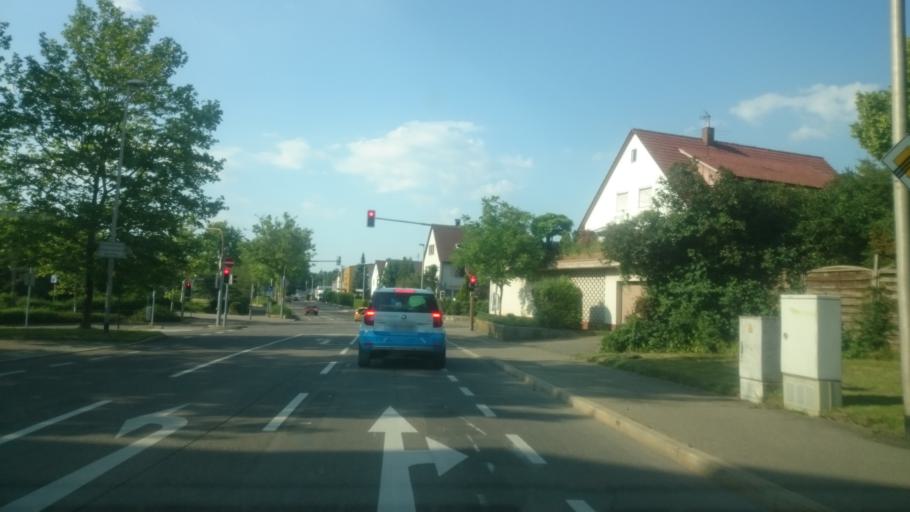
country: DE
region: Baden-Wuerttemberg
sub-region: Tuebingen Region
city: Mossingen
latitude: 48.4036
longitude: 9.0486
